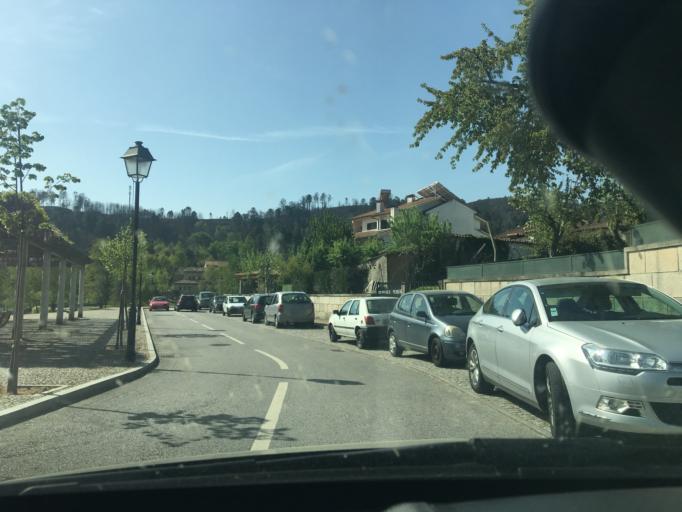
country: PT
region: Vila Real
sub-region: Boticas
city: Boticas
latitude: 41.6877
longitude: -7.6662
